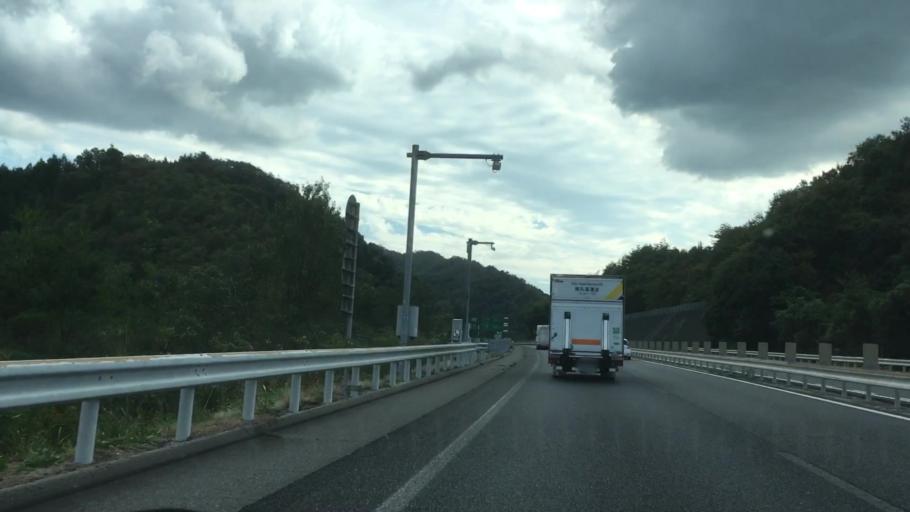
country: JP
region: Yamaguchi
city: Iwakuni
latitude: 34.1278
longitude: 132.1114
